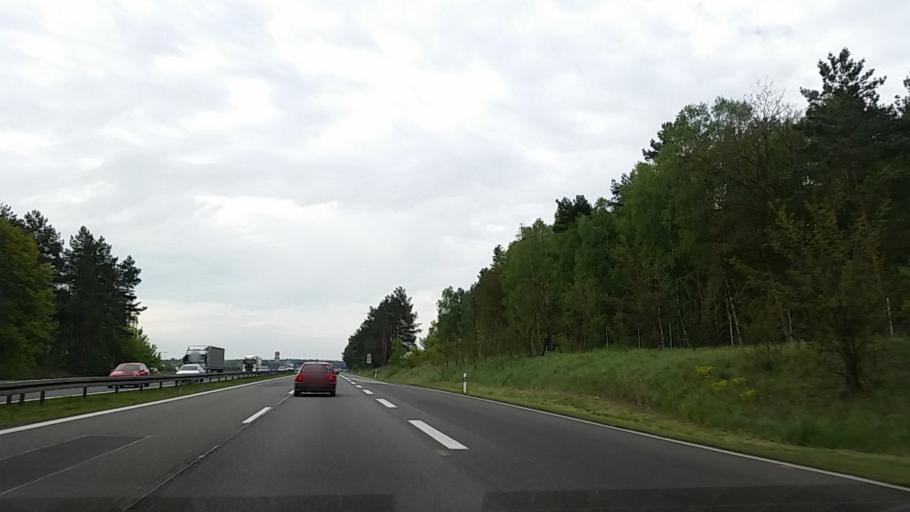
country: DE
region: Brandenburg
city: Wittstock
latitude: 53.0712
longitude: 12.5280
